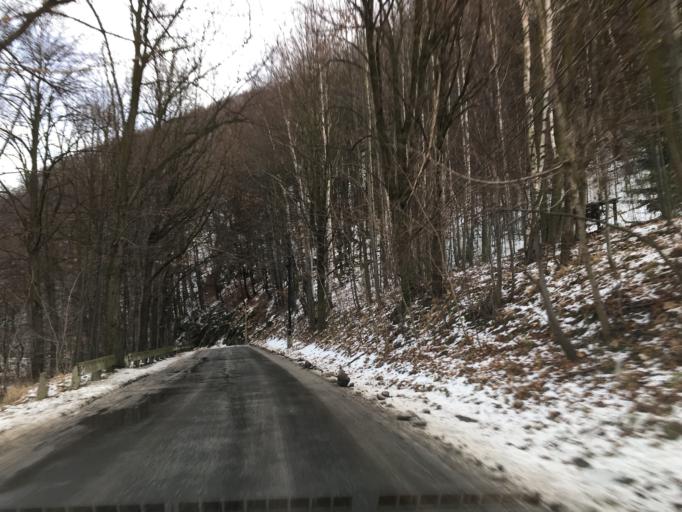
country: PL
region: Lower Silesian Voivodeship
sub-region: Powiat walbrzyski
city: Dziecmorowice
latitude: 50.7470
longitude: 16.4089
